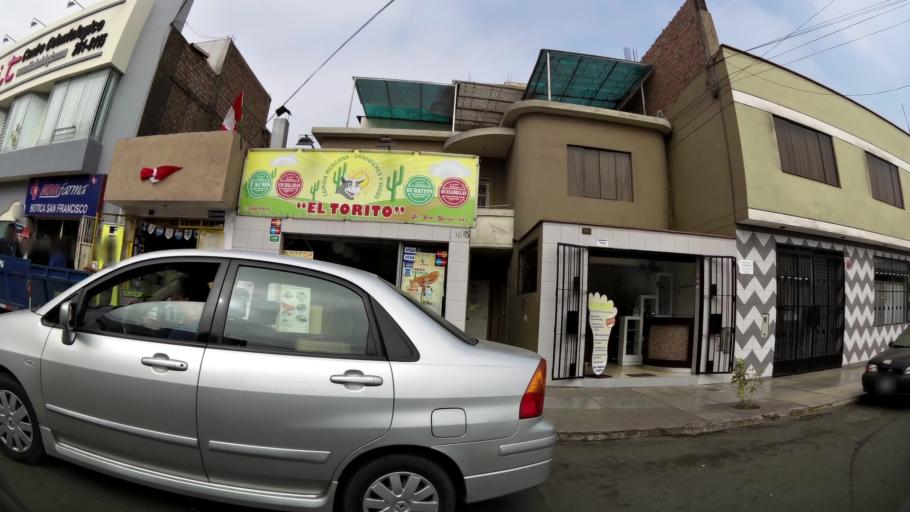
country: PE
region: Lima
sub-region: Lima
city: San Isidro
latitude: -12.0767
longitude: -77.0534
